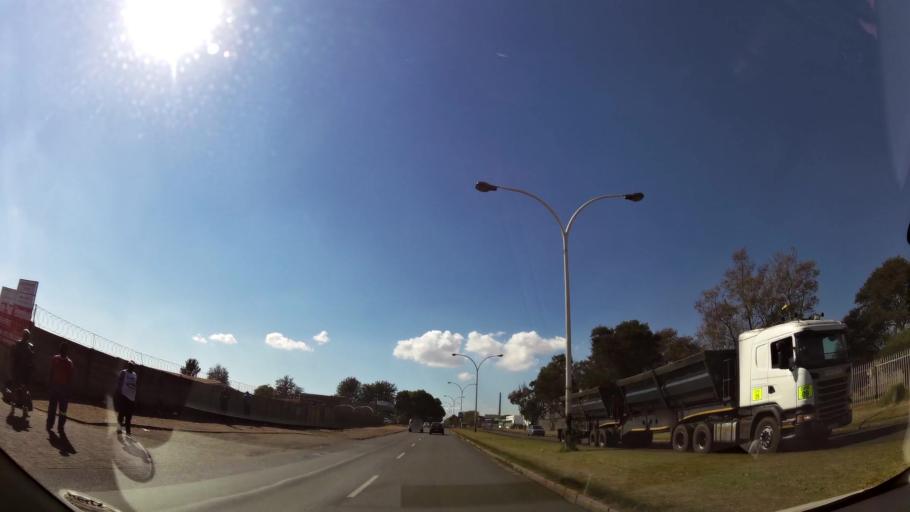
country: ZA
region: Mpumalanga
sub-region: Nkangala District Municipality
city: Witbank
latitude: -25.8702
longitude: 29.2127
